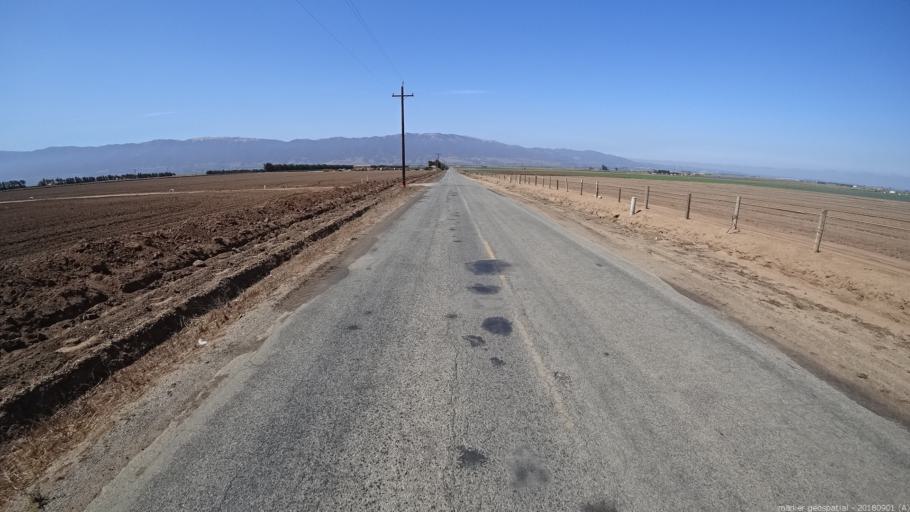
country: US
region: California
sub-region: Monterey County
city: Chualar
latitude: 36.5840
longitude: -121.4741
